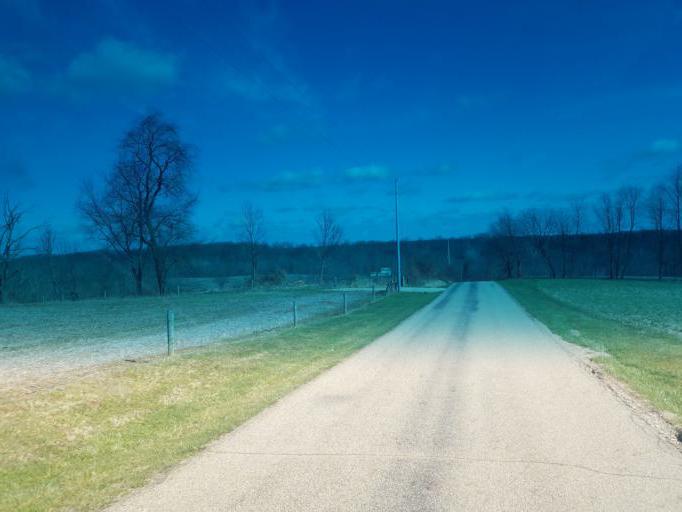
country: US
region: Ohio
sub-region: Knox County
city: Gambier
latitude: 40.3534
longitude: -82.3973
